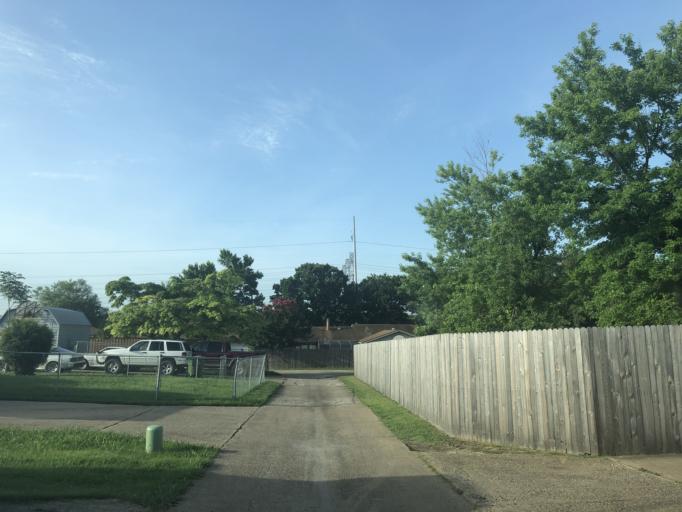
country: US
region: Texas
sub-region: Dallas County
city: Sunnyvale
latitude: 32.8356
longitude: -96.5883
